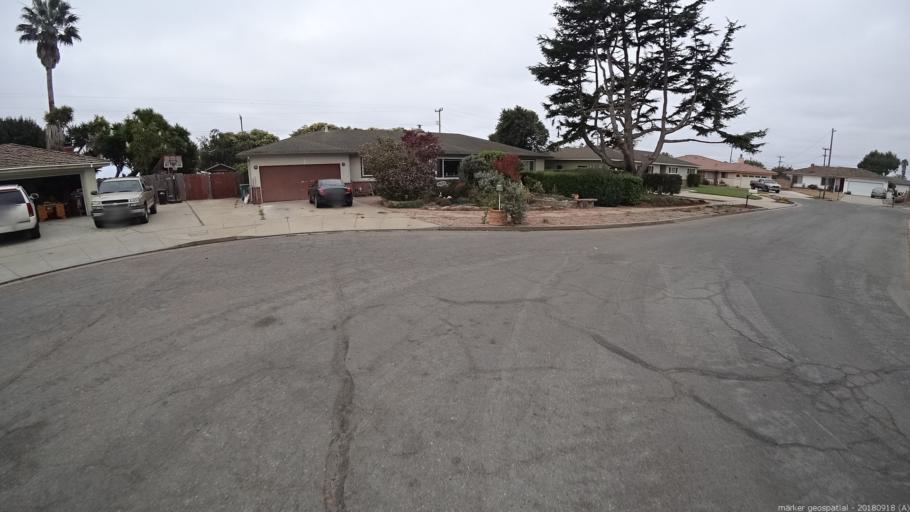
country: US
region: California
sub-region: Monterey County
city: Boronda
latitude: 36.7286
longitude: -121.6334
